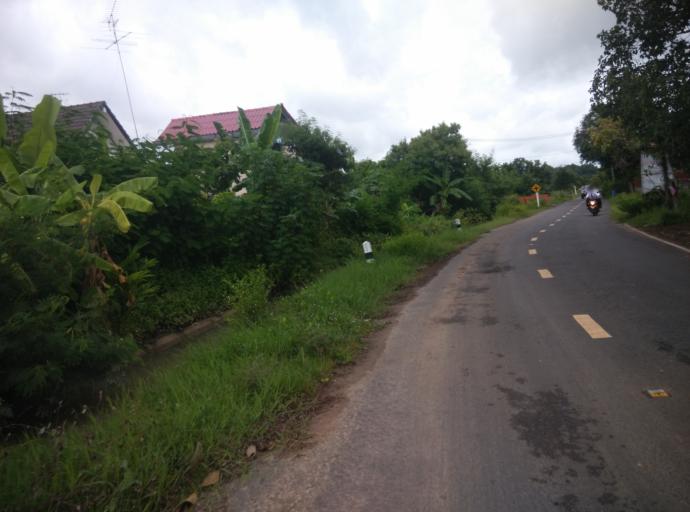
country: TH
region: Sisaket
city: Si Sa Ket
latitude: 15.1079
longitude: 104.3520
